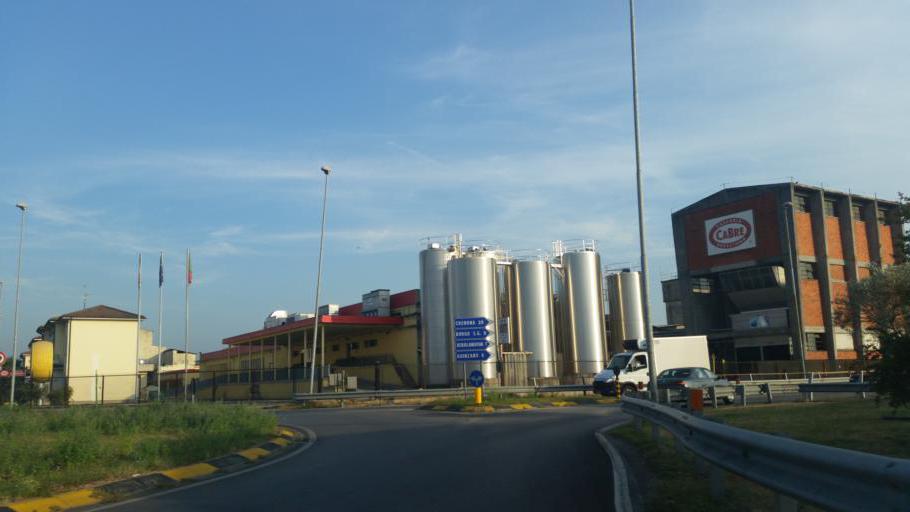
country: IT
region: Lombardy
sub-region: Provincia di Brescia
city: San Paolo
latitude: 45.3629
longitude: 10.0448
